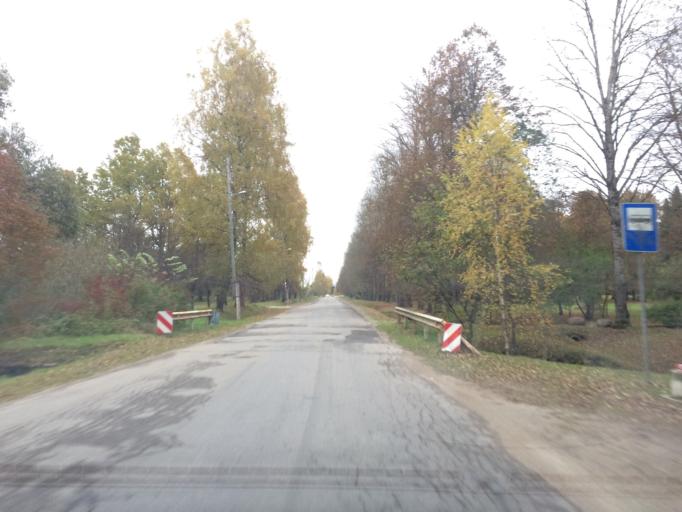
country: LV
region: Plavinu
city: Plavinas
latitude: 56.6180
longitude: 25.7558
